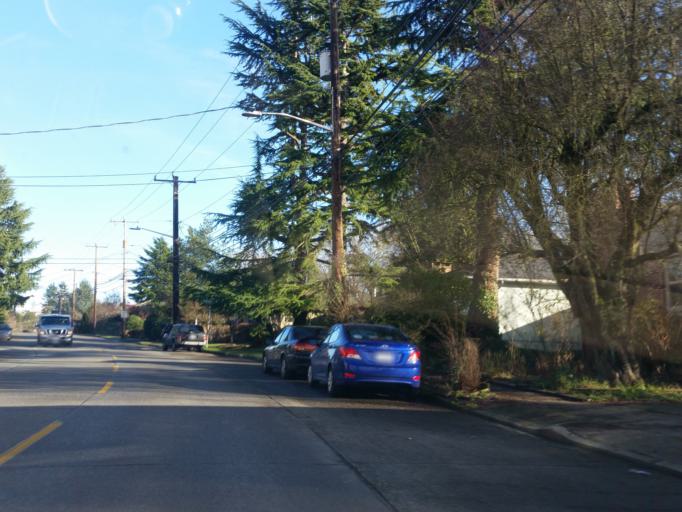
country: US
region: Washington
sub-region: King County
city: Yarrow Point
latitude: 47.6685
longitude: -122.2828
